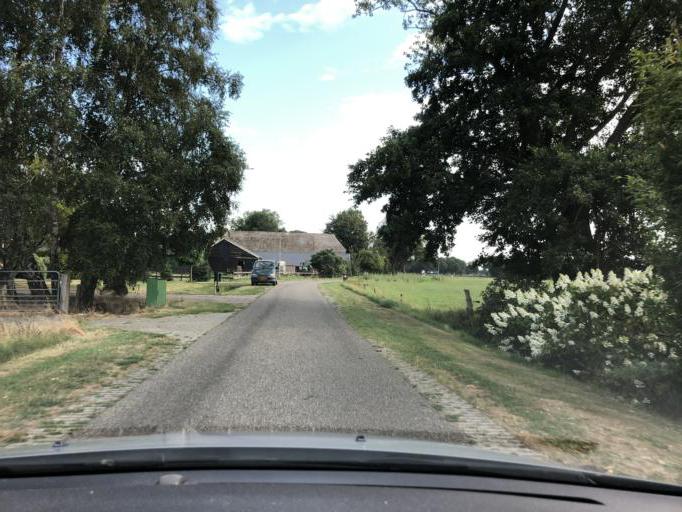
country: NL
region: Overijssel
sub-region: Gemeente Dalfsen
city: Dalfsen
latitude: 52.6003
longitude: 6.3460
